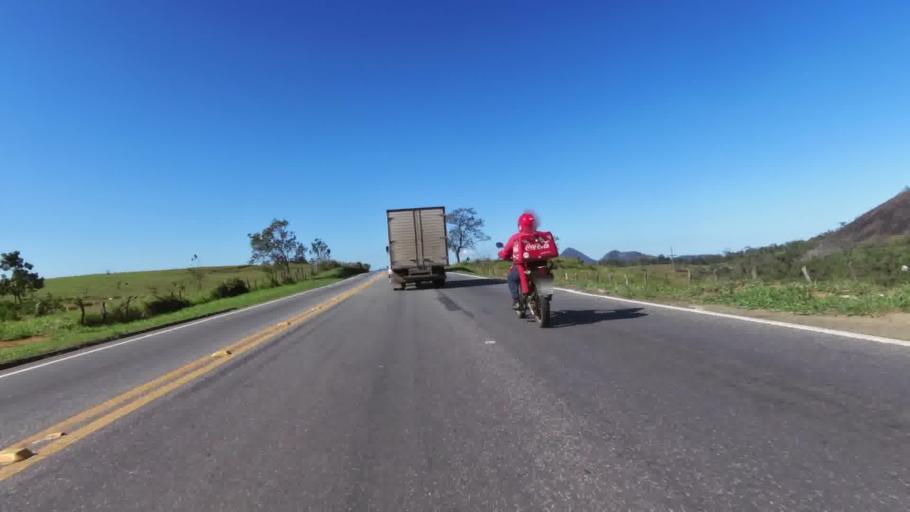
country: BR
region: Espirito Santo
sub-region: Alfredo Chaves
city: Alfredo Chaves
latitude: -20.6974
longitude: -40.7110
